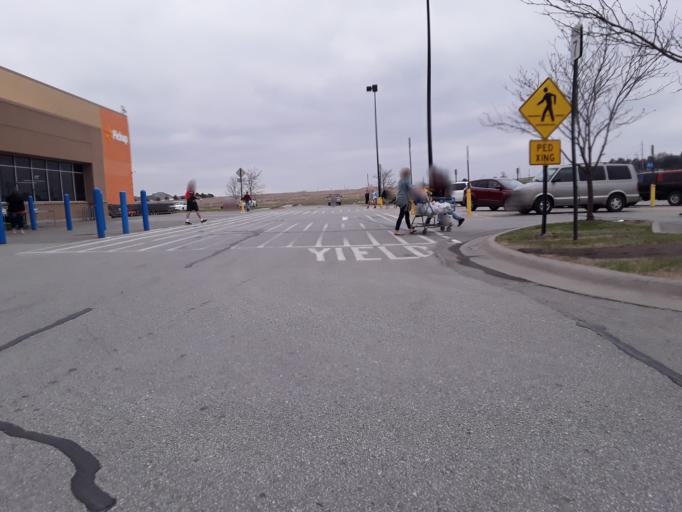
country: US
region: Nebraska
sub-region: Lancaster County
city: Lincoln
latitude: 40.8486
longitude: -96.6026
